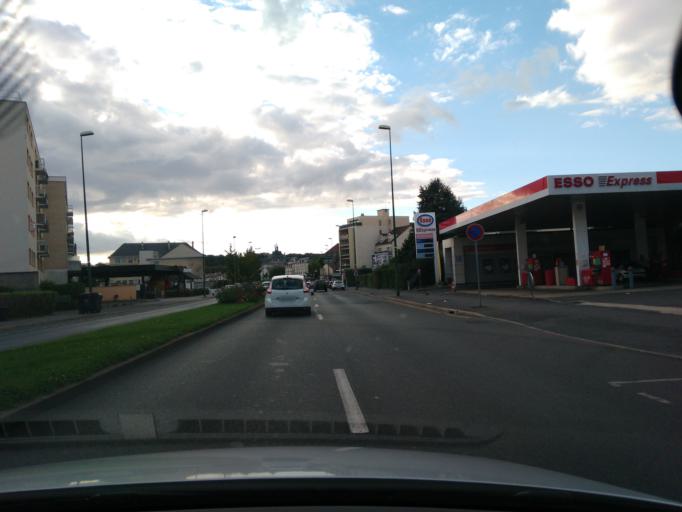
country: FR
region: Ile-de-France
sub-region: Departement de Seine-et-Marne
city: Meaux
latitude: 48.9569
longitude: 2.8852
